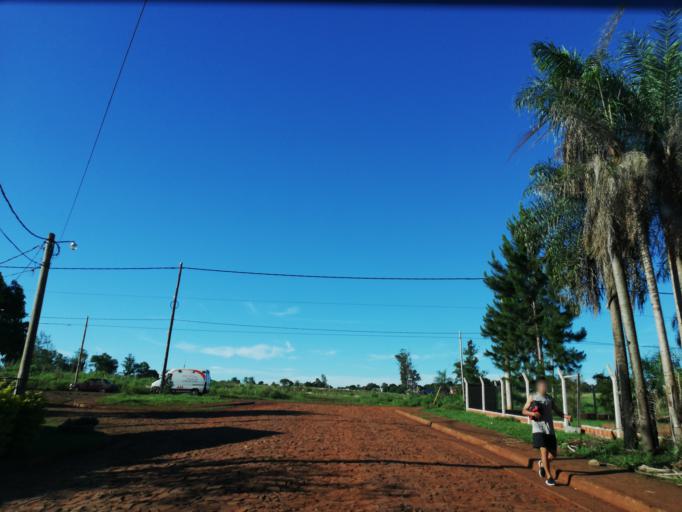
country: AR
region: Misiones
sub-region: Departamento de Capital
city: Posadas
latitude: -27.4341
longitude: -55.9352
